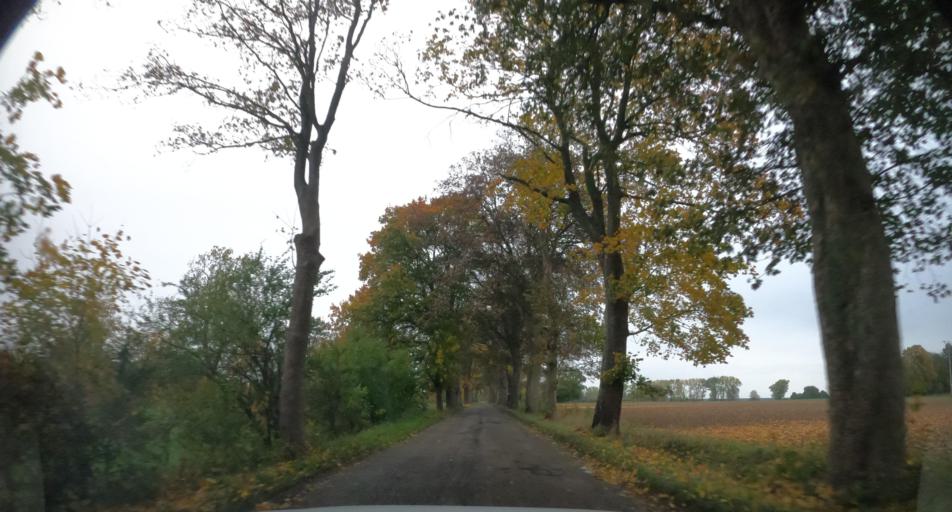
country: PL
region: West Pomeranian Voivodeship
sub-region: Powiat kamienski
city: Wolin
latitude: 53.9063
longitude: 14.6207
